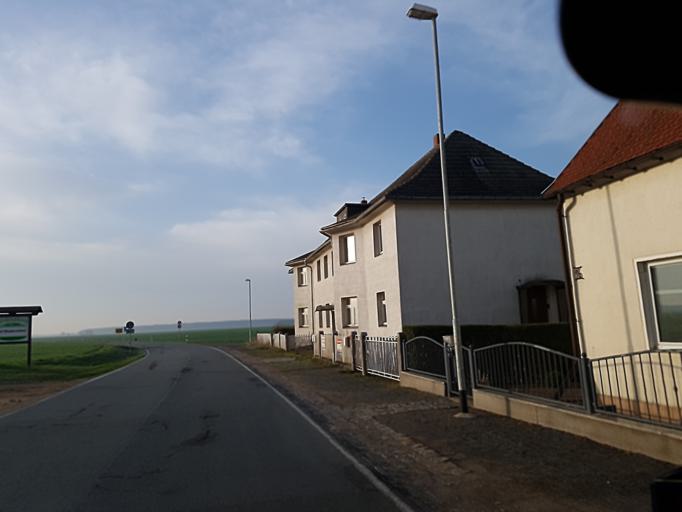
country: DE
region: Brandenburg
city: Muhlberg
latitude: 51.4026
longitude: 13.2593
